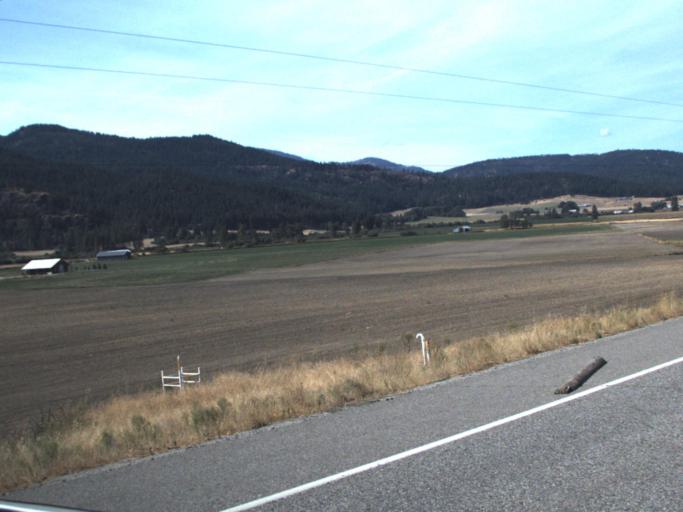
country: US
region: Washington
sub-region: Stevens County
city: Chewelah
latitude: 48.2985
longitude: -117.7564
